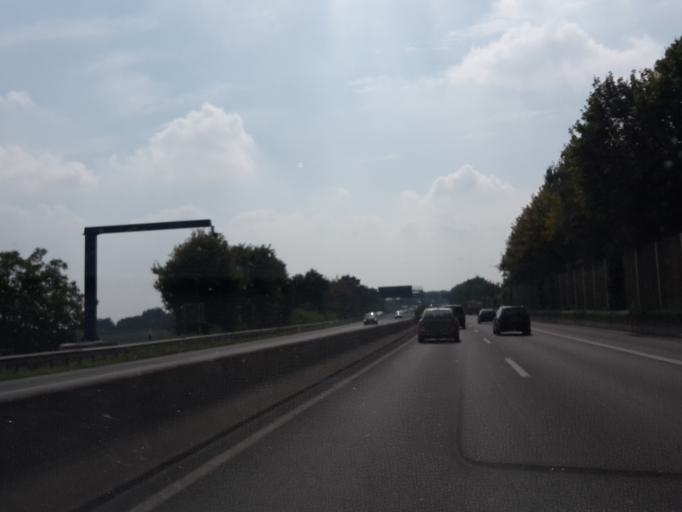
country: DE
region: Rheinland-Pfalz
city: Klein-Winternheim
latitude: 49.9579
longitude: 8.2314
